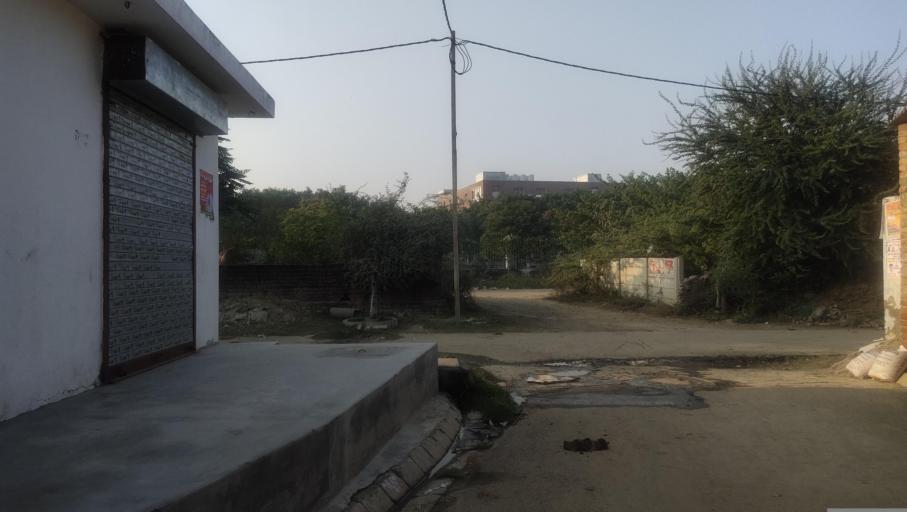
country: IN
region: Uttar Pradesh
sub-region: Lucknow District
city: Goshainganj
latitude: 26.7912
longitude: 81.0123
